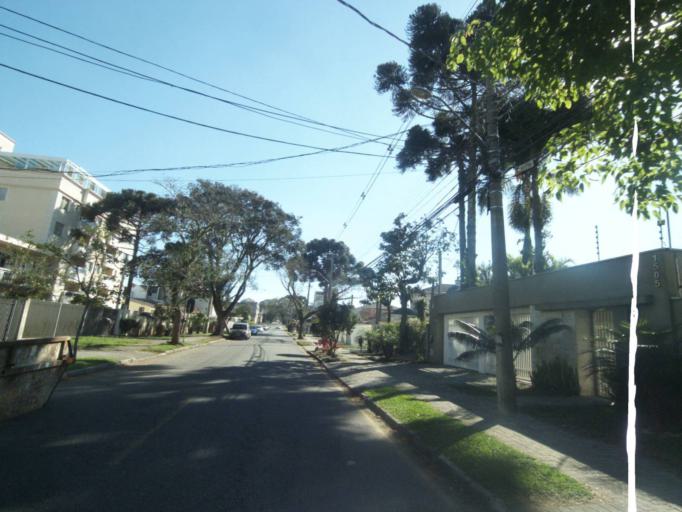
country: BR
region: Parana
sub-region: Curitiba
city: Curitiba
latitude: -25.3946
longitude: -49.2337
